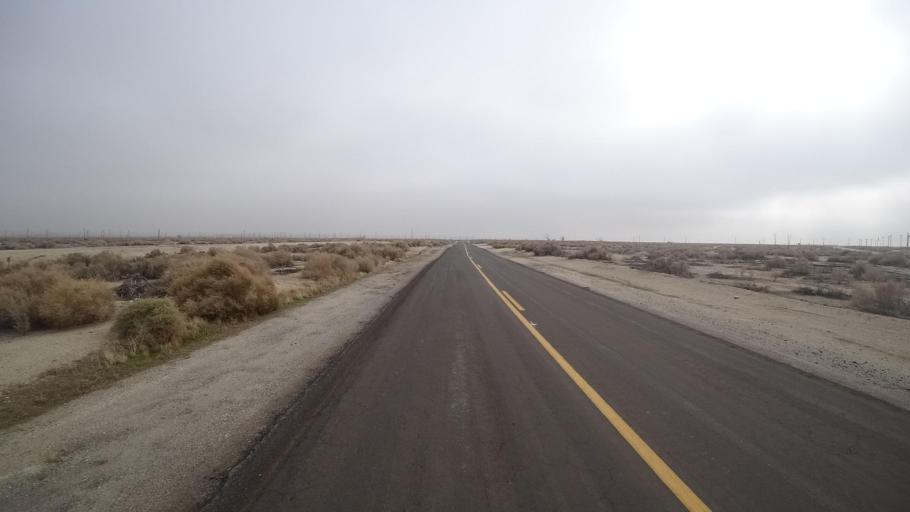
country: US
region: California
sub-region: Kern County
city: Maricopa
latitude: 35.0809
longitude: -119.3832
